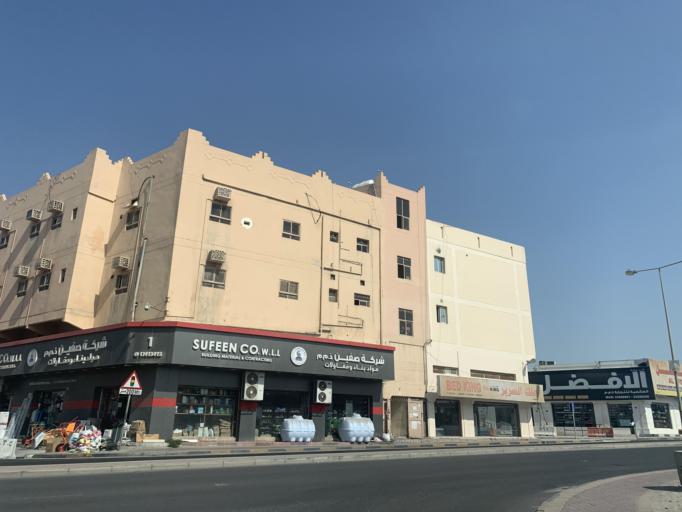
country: BH
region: Central Governorate
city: Madinat Hamad
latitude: 26.1402
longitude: 50.4976
